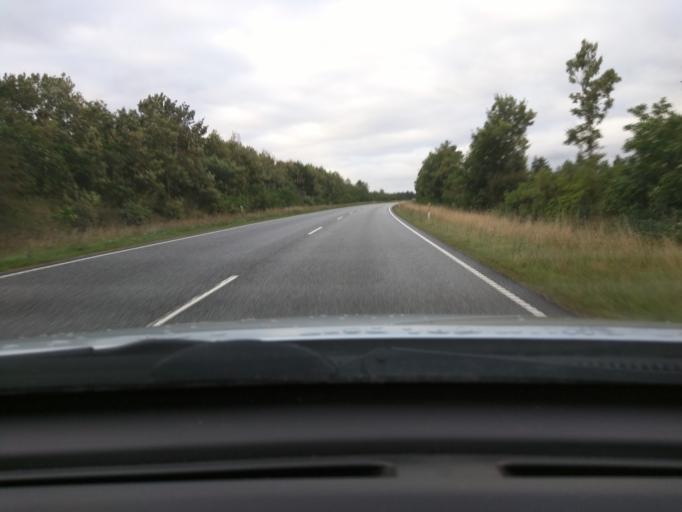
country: DK
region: Central Jutland
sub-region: Ikast-Brande Kommune
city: Bording Kirkeby
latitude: 56.2343
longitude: 9.3234
